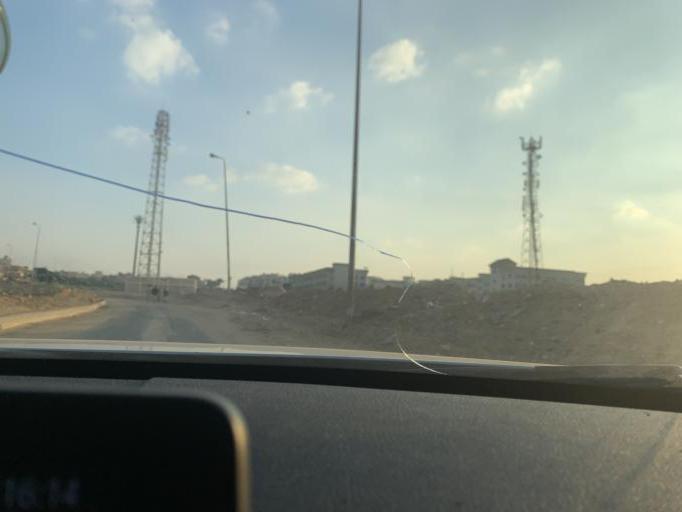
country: EG
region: Muhafazat al Qalyubiyah
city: Al Khankah
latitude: 30.0220
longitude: 31.4813
